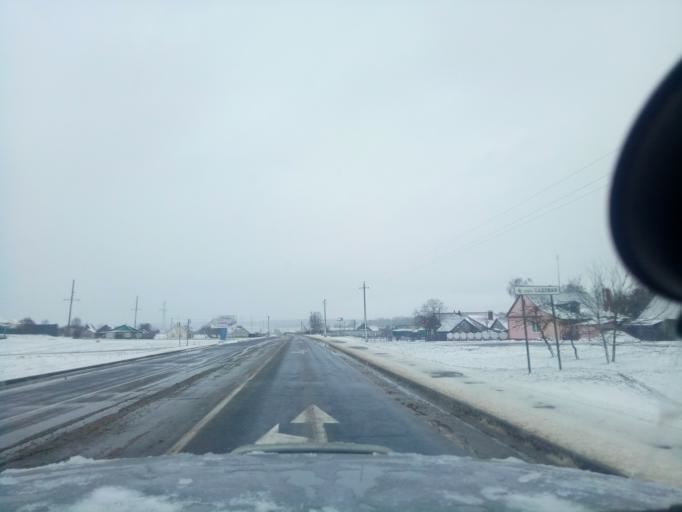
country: BY
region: Minsk
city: Nyasvizh
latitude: 53.2094
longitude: 26.6600
